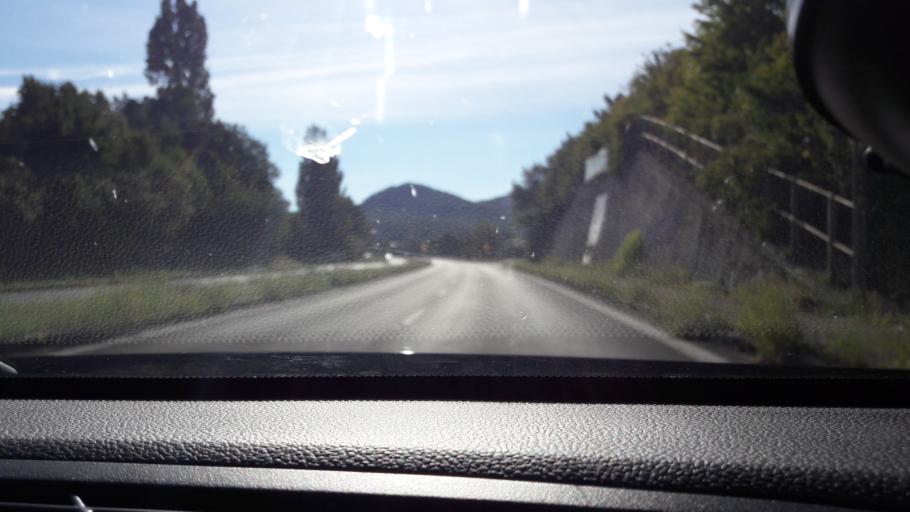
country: SK
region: Kosicky
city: Vinne
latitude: 48.8098
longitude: 22.0130
